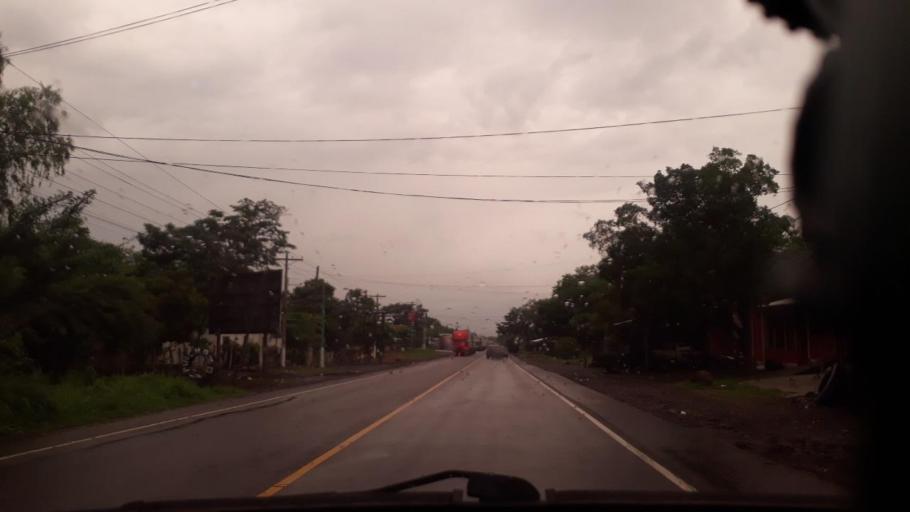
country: SV
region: Ahuachapan
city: San Francisco Menendez
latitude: 13.8809
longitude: -90.1001
